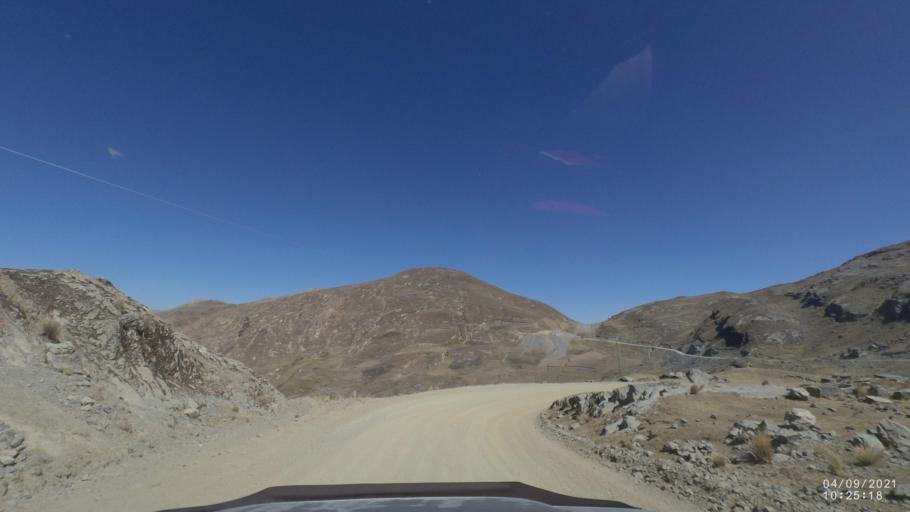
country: BO
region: Cochabamba
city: Sipe Sipe
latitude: -17.3057
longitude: -66.4370
